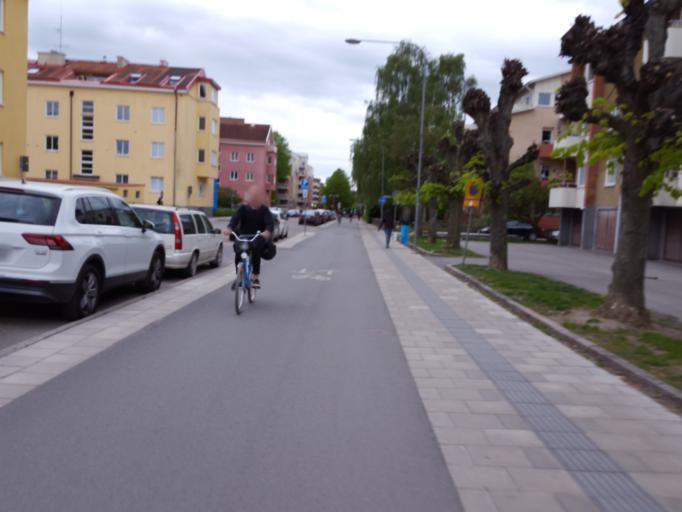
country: SE
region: Uppsala
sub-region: Uppsala Kommun
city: Uppsala
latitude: 59.8650
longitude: 17.6491
